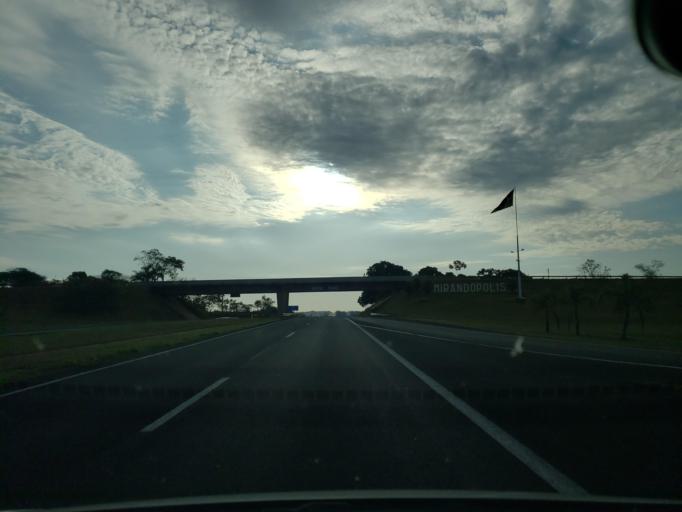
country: BR
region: Sao Paulo
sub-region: Mirandopolis
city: Mirandopolis
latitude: -21.0869
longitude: -51.0616
